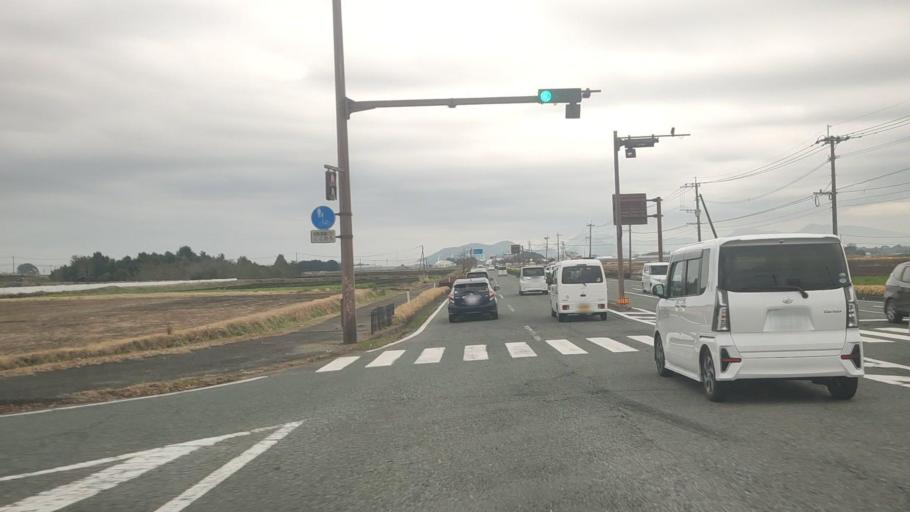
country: JP
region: Kumamoto
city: Ozu
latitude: 32.8470
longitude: 130.8344
